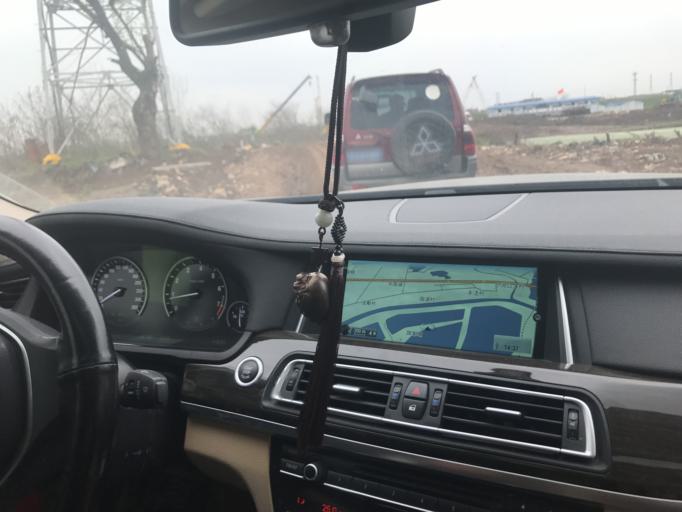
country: CN
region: Hubei
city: Zhanjiaji
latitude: 30.6835
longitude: 114.3420
